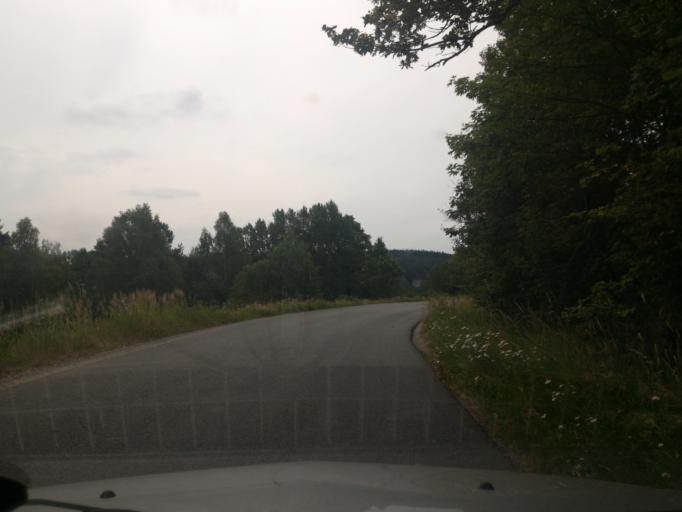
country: CZ
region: Vysocina
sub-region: Okres Jihlava
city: Telc
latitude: 49.2159
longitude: 15.3941
